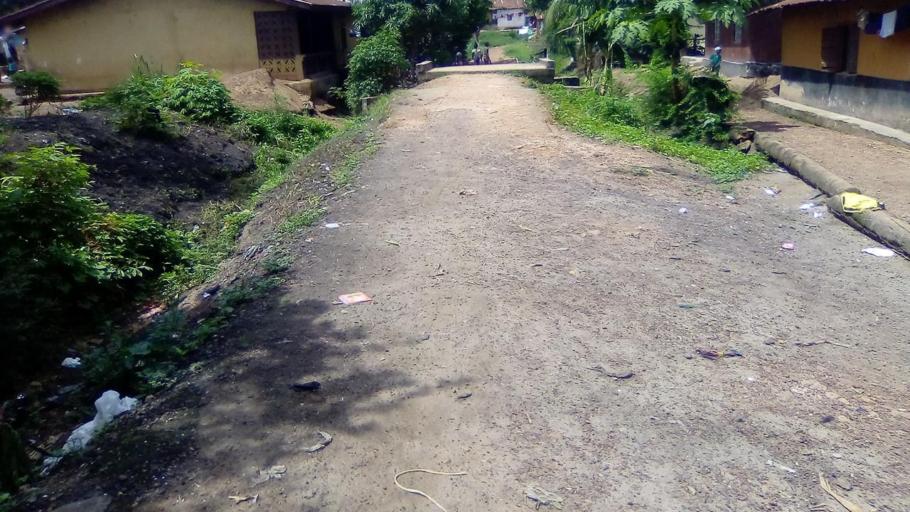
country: SL
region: Southern Province
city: Bo
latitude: 7.9668
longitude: -11.7326
